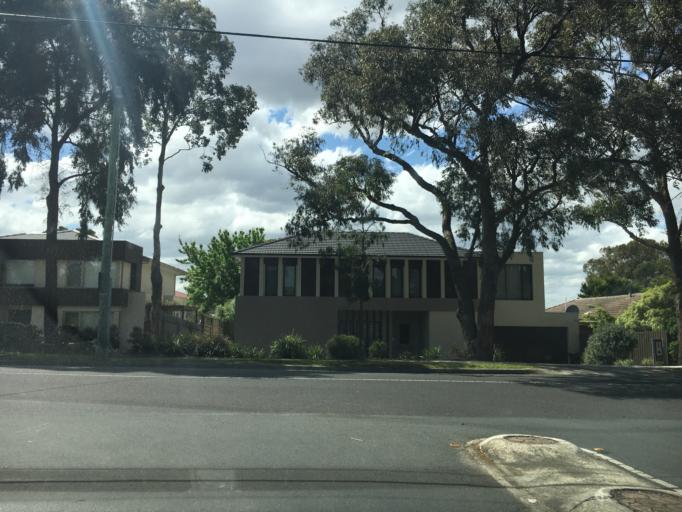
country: AU
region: Victoria
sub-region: Whitehorse
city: Vermont South
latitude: -37.8839
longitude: 145.1819
